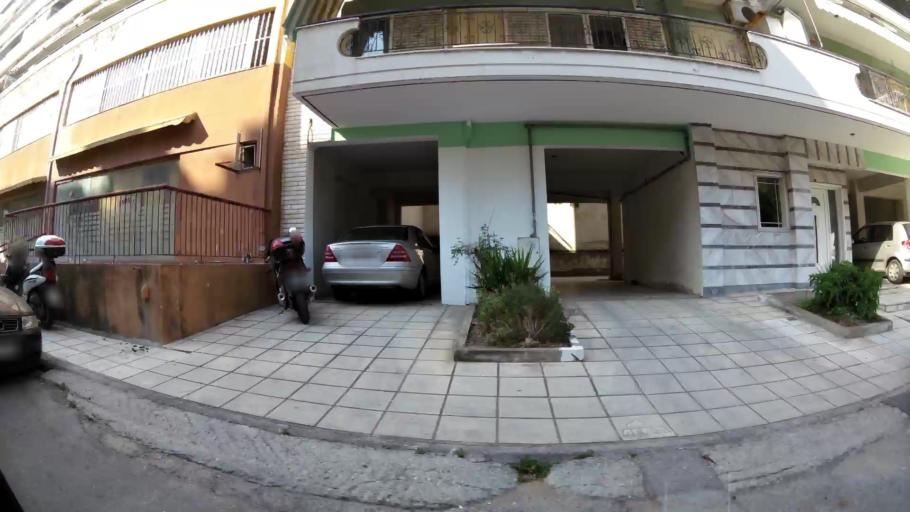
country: GR
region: Central Macedonia
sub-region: Nomos Thessalonikis
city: Sykies
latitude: 40.6561
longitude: 22.9597
